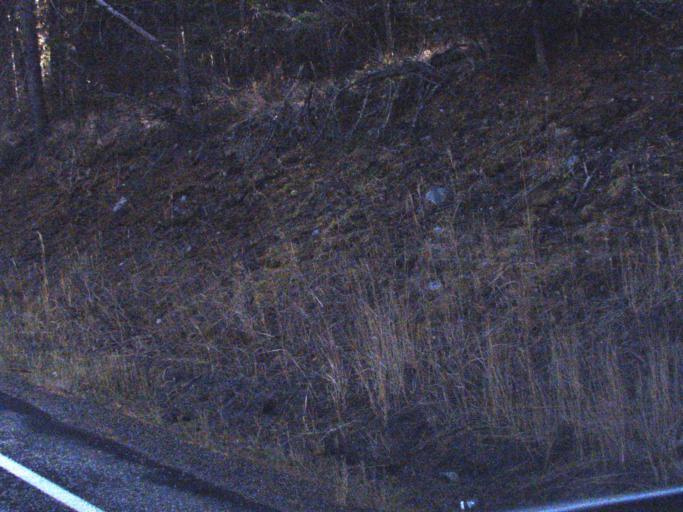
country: US
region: Washington
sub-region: Ferry County
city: Republic
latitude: 48.6128
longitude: -118.5817
